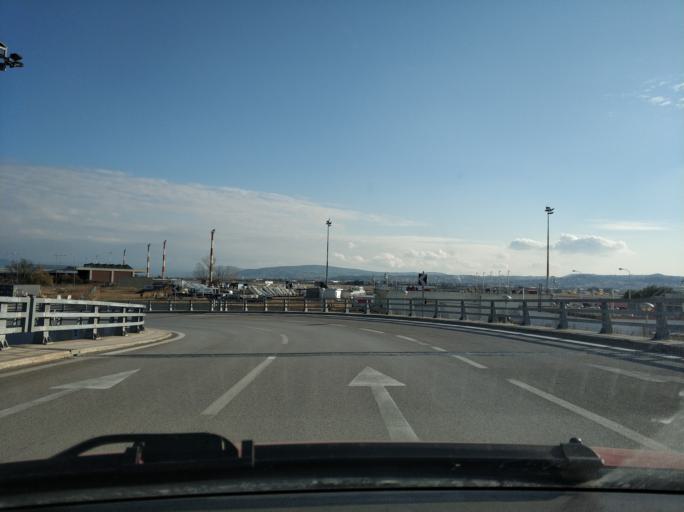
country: GR
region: Central Macedonia
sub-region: Nomos Thessalonikis
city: Neo Rysi
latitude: 40.5233
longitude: 22.9778
